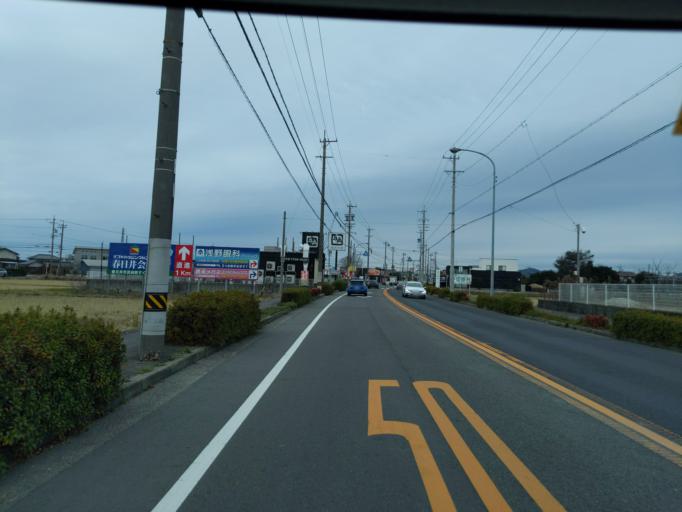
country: JP
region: Aichi
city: Kasugai
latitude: 35.2646
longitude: 136.9724
